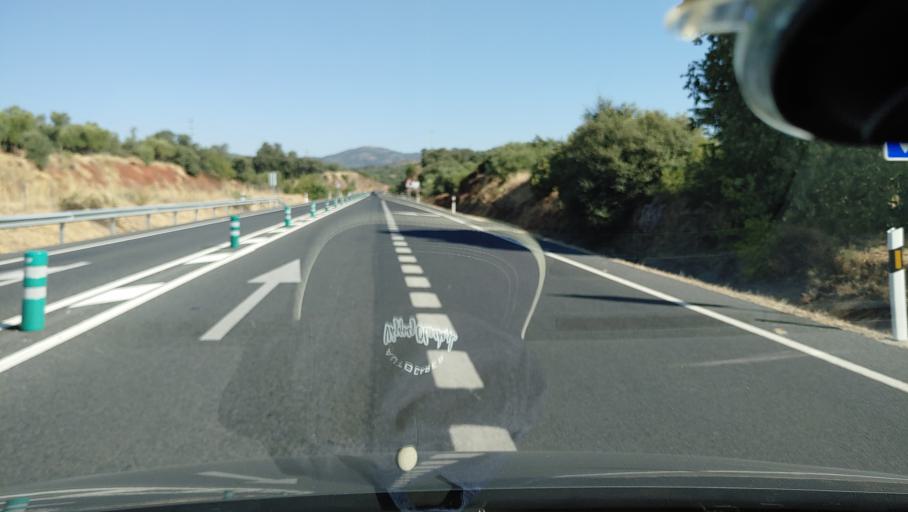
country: ES
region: Andalusia
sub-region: Province of Cordoba
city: Cordoba
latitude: 37.9242
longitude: -4.7656
